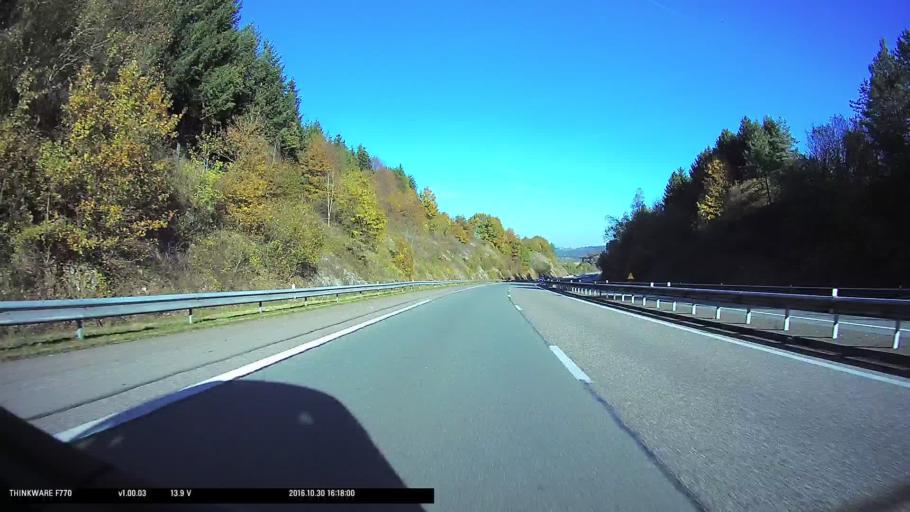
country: FR
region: Franche-Comte
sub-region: Departement du Doubs
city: Clerval
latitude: 47.4117
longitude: 6.5069
